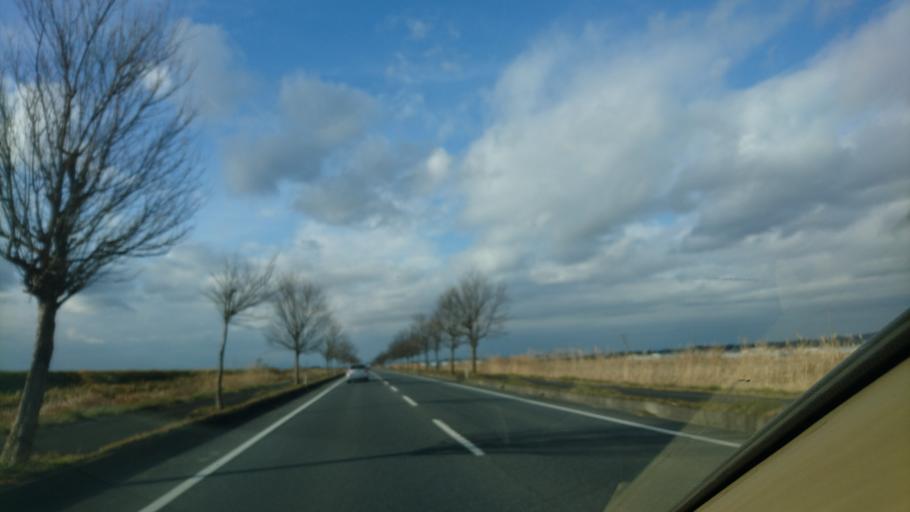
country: JP
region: Miyagi
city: Wakuya
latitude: 38.5383
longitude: 141.1159
